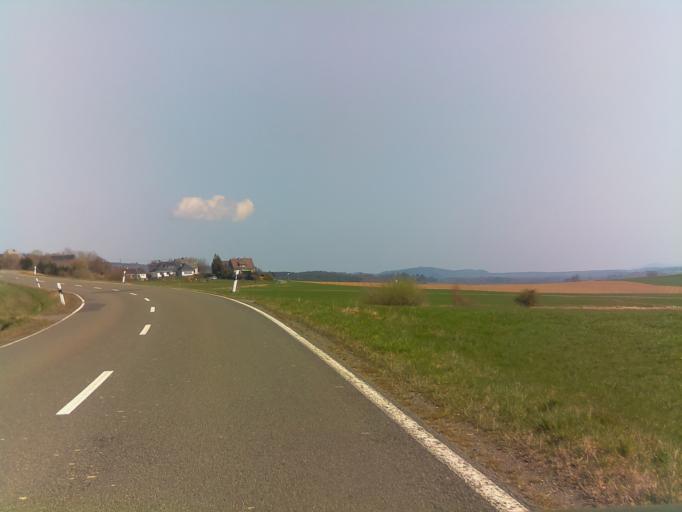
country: DE
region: Rheinland-Pfalz
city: Hattgenstein
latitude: 49.6920
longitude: 7.1577
